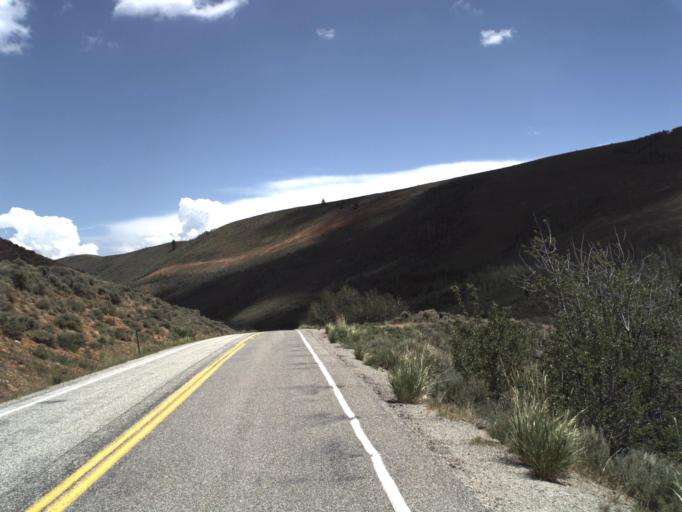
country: US
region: Utah
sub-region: Rich County
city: Randolph
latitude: 41.4819
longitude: -111.3744
